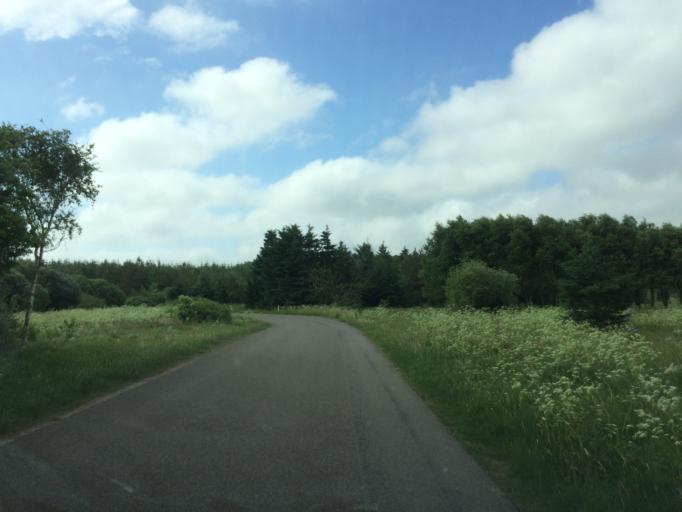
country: DK
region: Central Jutland
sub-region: Holstebro Kommune
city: Ulfborg
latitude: 56.2248
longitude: 8.4346
